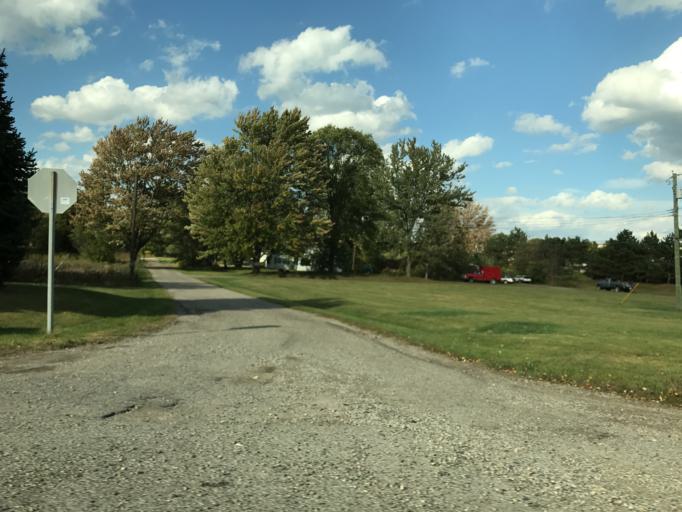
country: US
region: Michigan
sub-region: Oakland County
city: Wixom
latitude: 42.5041
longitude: -83.5805
